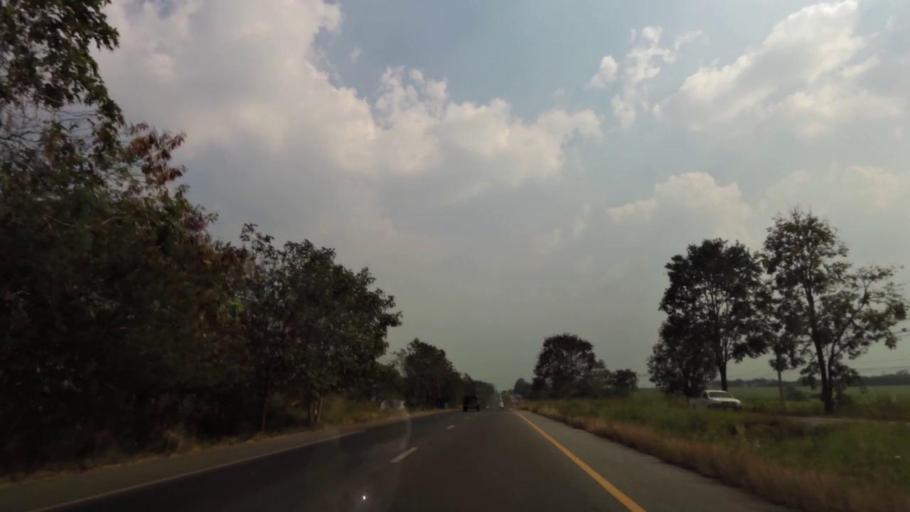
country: TH
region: Chon Buri
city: Nong Yai
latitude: 13.1463
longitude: 101.3341
